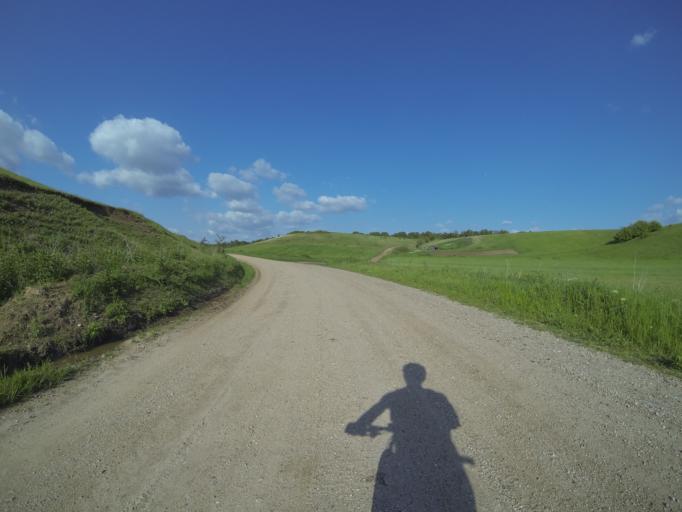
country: RO
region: Dolj
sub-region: Comuna Verbita
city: Verbita
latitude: 44.2849
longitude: 23.1955
